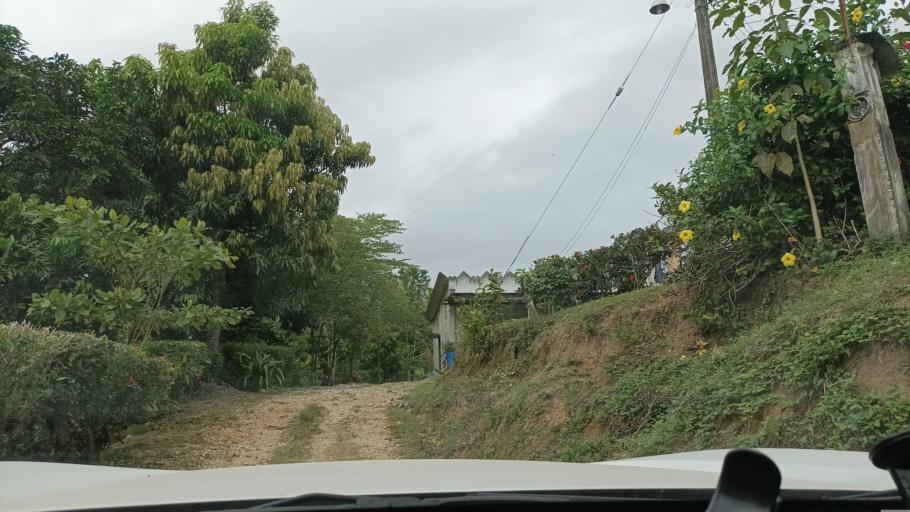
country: MX
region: Veracruz
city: Hidalgotitlan
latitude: 17.8123
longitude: -94.5376
